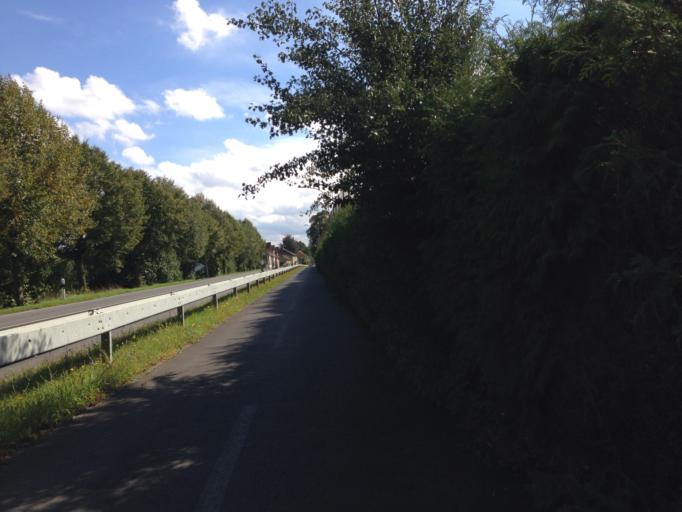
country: DE
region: Hesse
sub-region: Regierungsbezirk Giessen
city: Hungen
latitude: 50.4794
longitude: 8.9016
